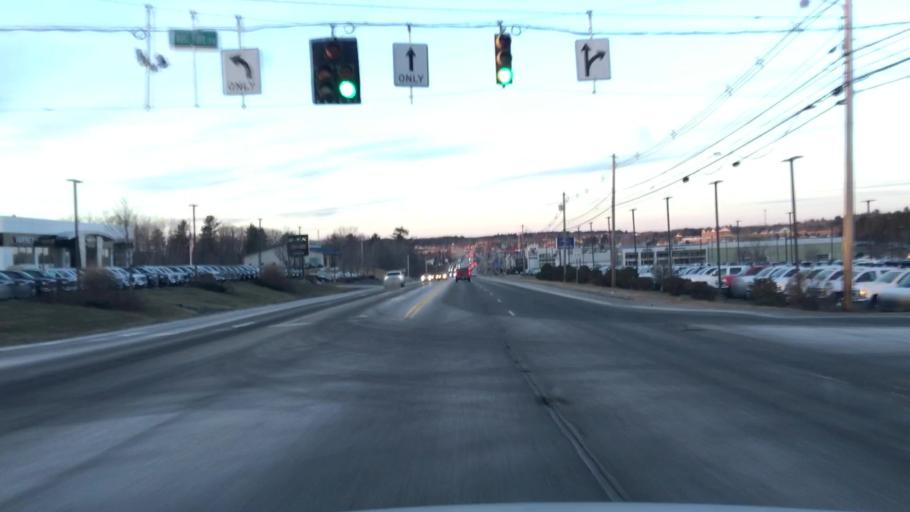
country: US
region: Maine
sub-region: Penobscot County
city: Brewer
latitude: 44.8225
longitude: -68.7396
